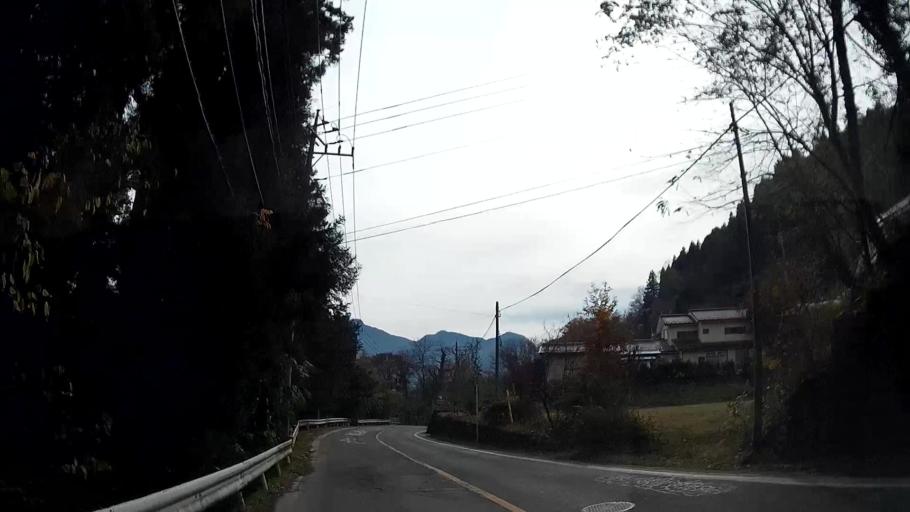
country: JP
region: Saitama
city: Chichibu
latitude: 35.9824
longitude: 139.0541
